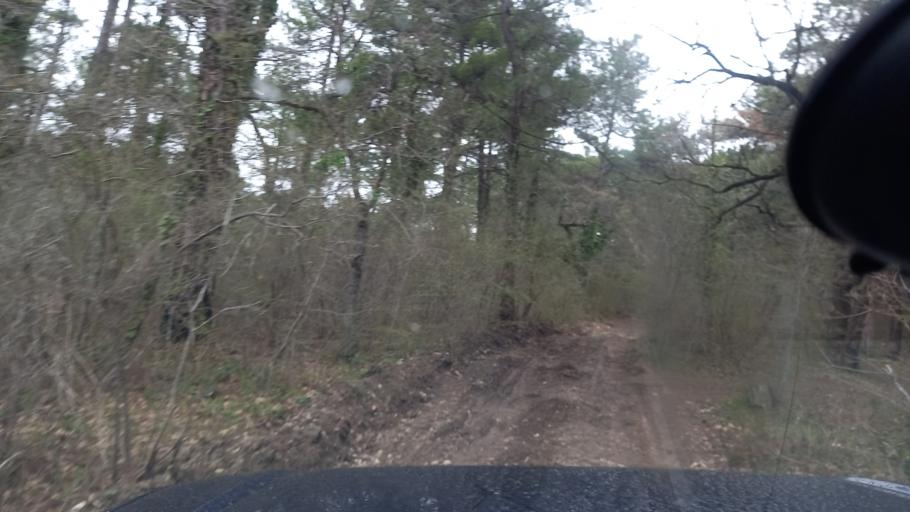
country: RU
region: Krasnodarskiy
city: Arkhipo-Osipovka
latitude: 44.3687
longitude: 38.4723
